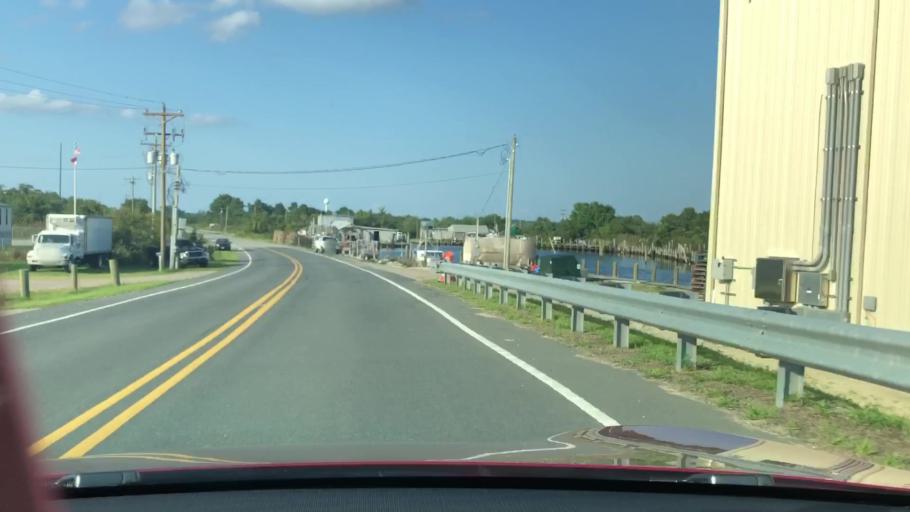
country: US
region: North Carolina
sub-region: Dare County
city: Wanchese
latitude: 35.6972
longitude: -75.7734
